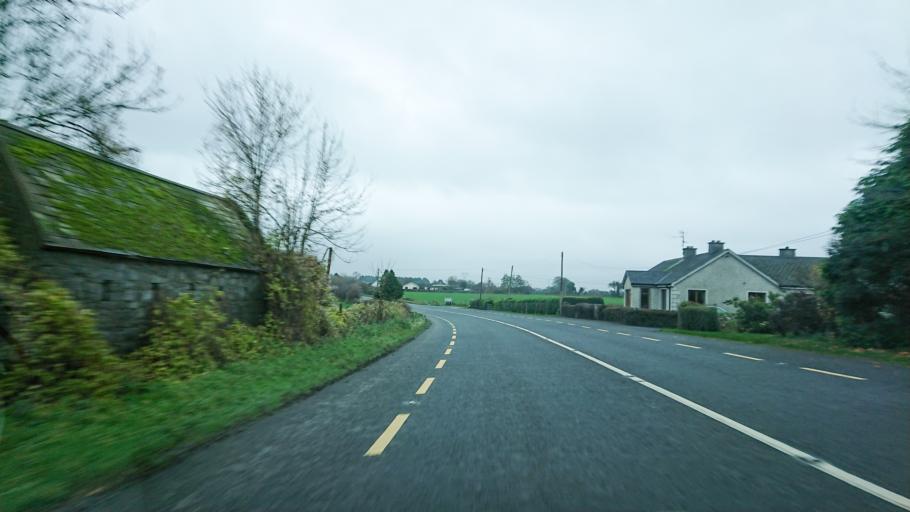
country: IE
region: Leinster
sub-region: Kilkenny
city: Mooncoin
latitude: 52.2819
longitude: -7.2011
